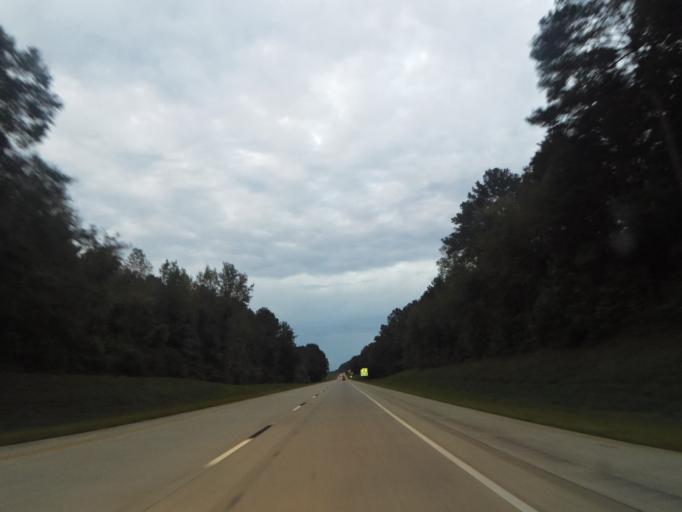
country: US
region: Alabama
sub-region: Etowah County
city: Gadsden
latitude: 34.0569
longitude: -86.0389
